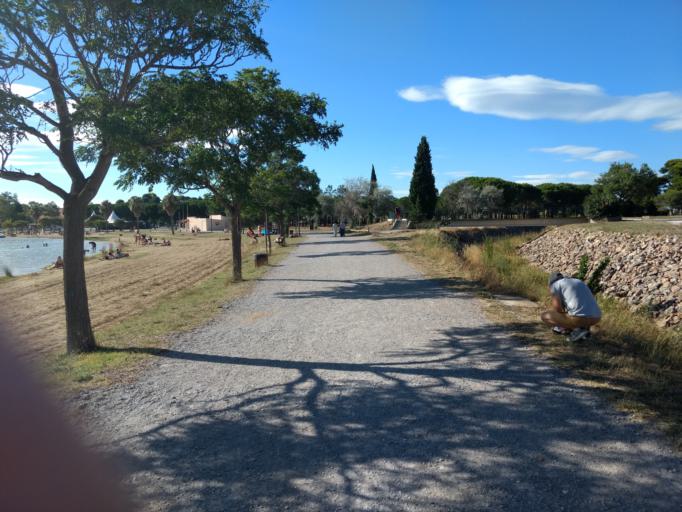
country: FR
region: Languedoc-Roussillon
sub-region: Departement des Pyrenees-Orientales
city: Villeneuve-de-la-Raho
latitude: 42.6394
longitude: 2.9085
